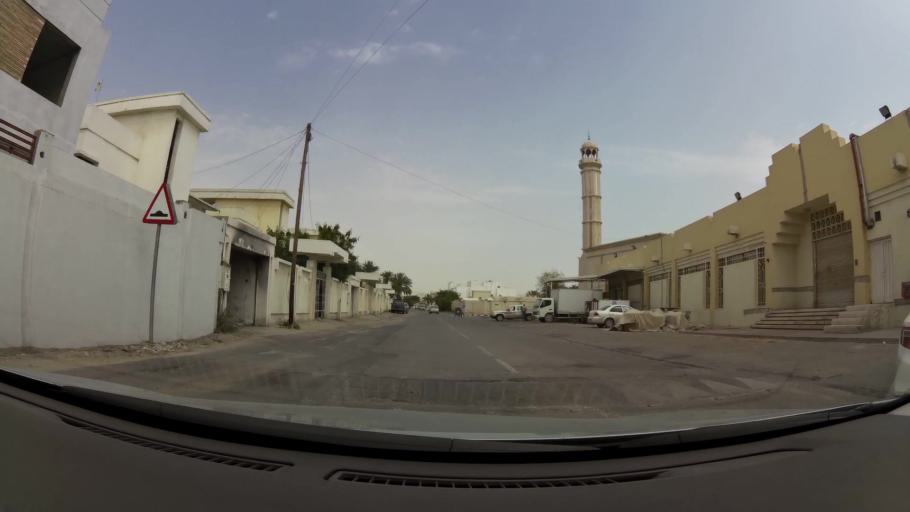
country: QA
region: Baladiyat ad Dawhah
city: Doha
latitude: 25.3032
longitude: 51.4897
